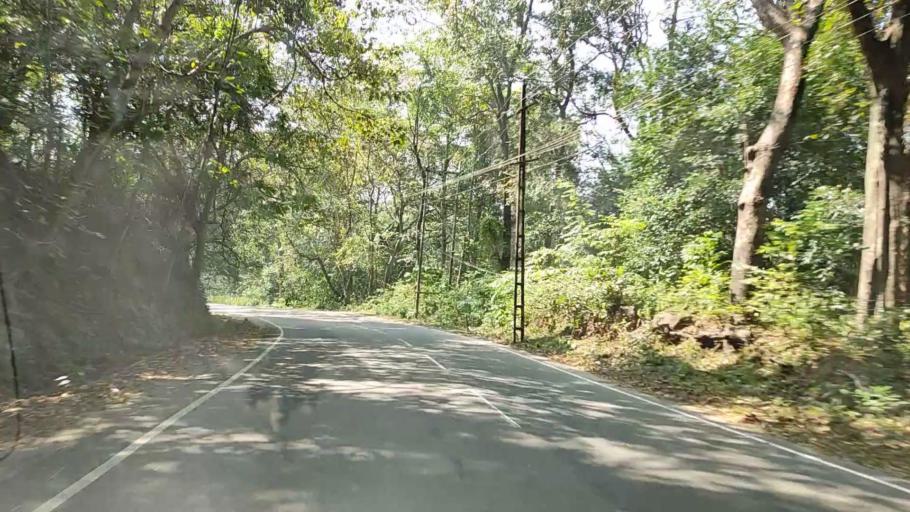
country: IN
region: Kerala
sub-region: Kollam
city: Punalur
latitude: 8.9588
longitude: 77.0667
